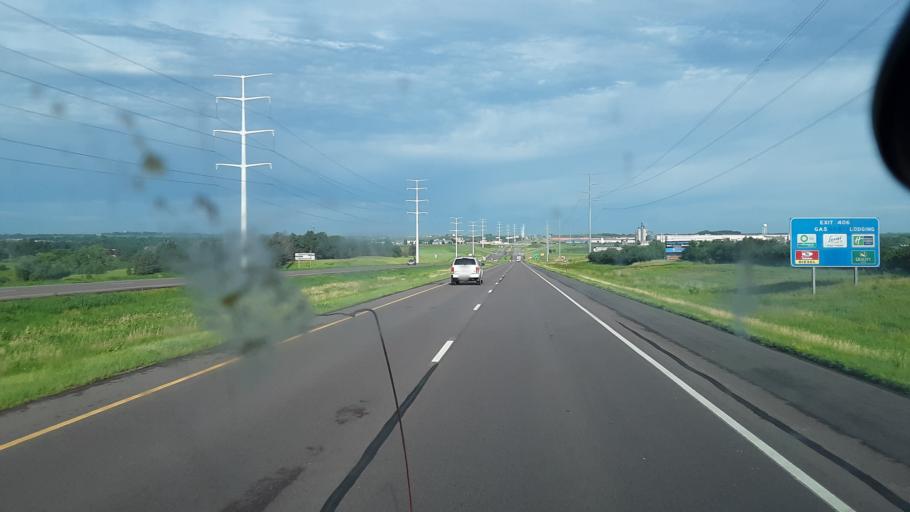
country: US
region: South Dakota
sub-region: Minnehaha County
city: Brandon
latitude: 43.6086
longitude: -96.5548
